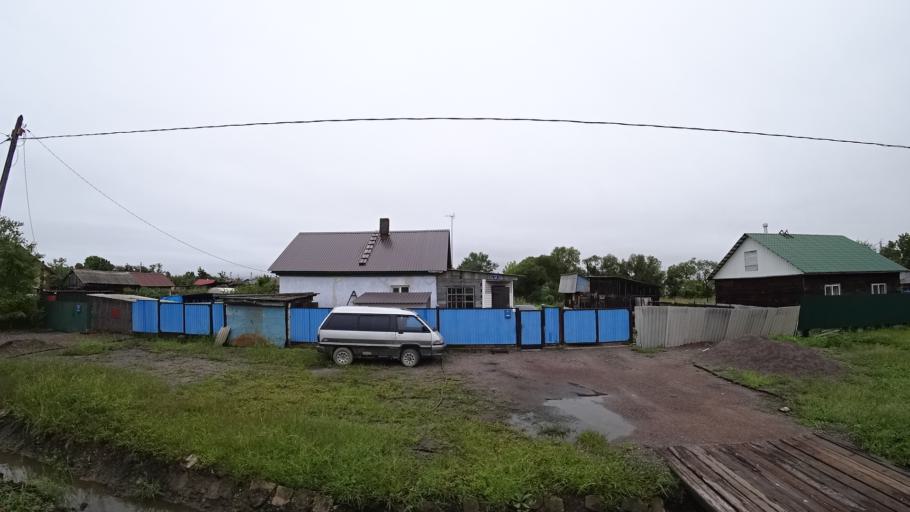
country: RU
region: Primorskiy
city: Monastyrishche
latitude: 44.2094
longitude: 132.4337
